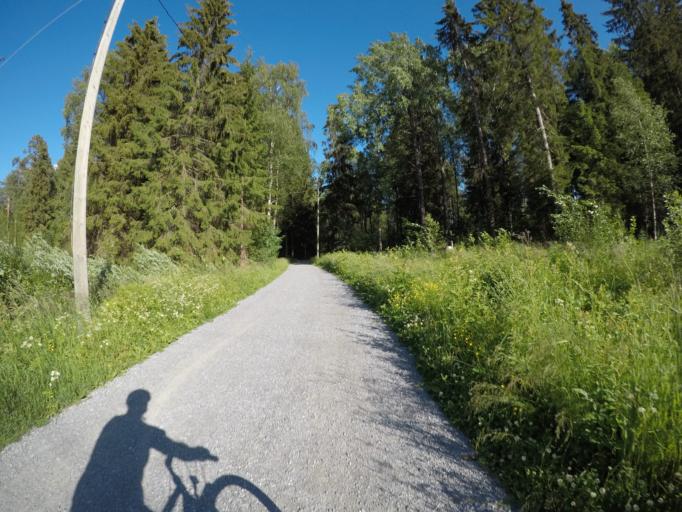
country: FI
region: Haeme
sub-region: Haemeenlinna
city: Haemeenlinna
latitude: 61.0192
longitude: 24.4885
